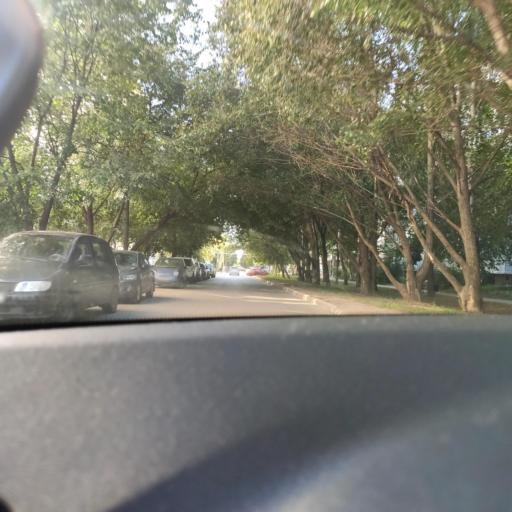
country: RU
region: Samara
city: Volzhskiy
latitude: 53.3508
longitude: 50.2122
